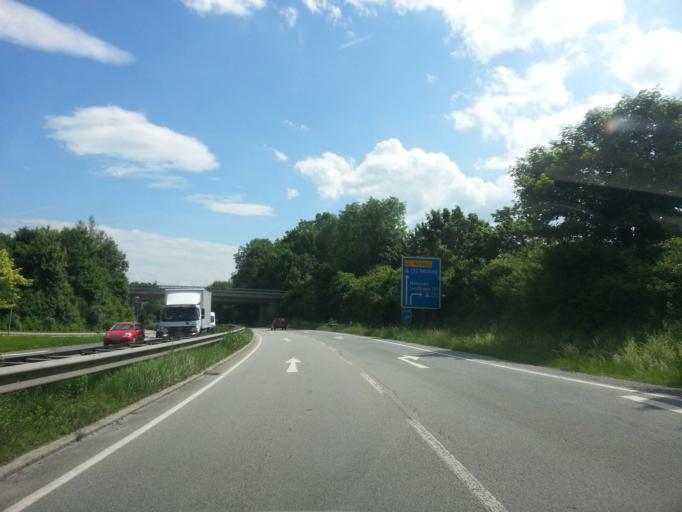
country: DE
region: Bavaria
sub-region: Upper Bavaria
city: Raubling
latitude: 47.8128
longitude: 12.1186
